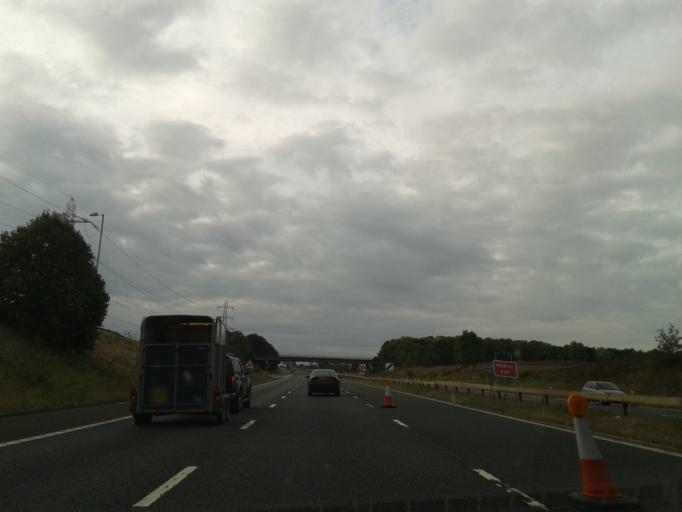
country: GB
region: England
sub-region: Cumbria
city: Scotby
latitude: 54.8948
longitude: -2.8866
